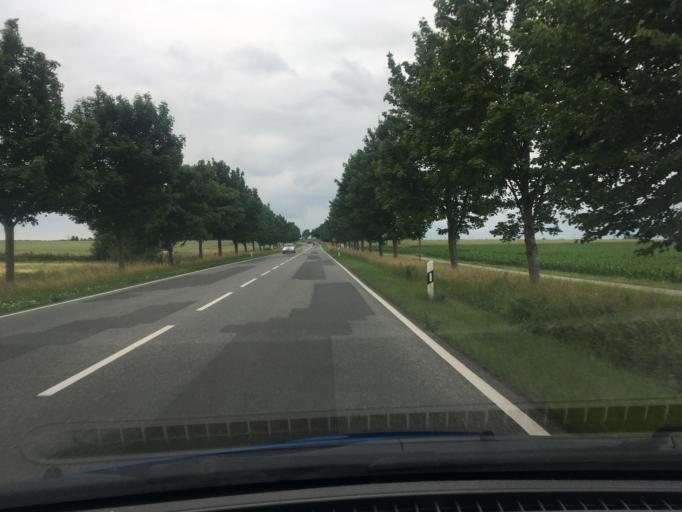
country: DE
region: Mecklenburg-Vorpommern
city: Stralendorf
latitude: 53.5423
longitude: 11.3097
